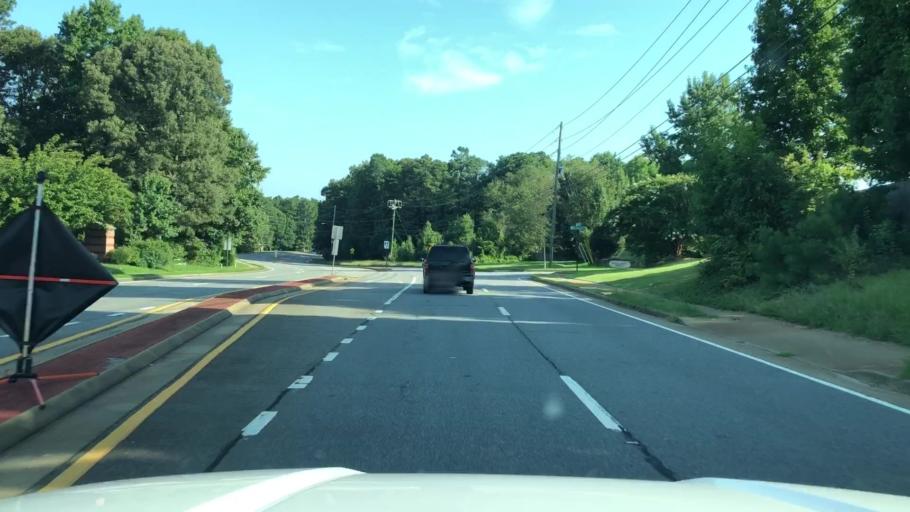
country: US
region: Georgia
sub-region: Cobb County
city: Kennesaw
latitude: 34.0743
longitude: -84.5871
